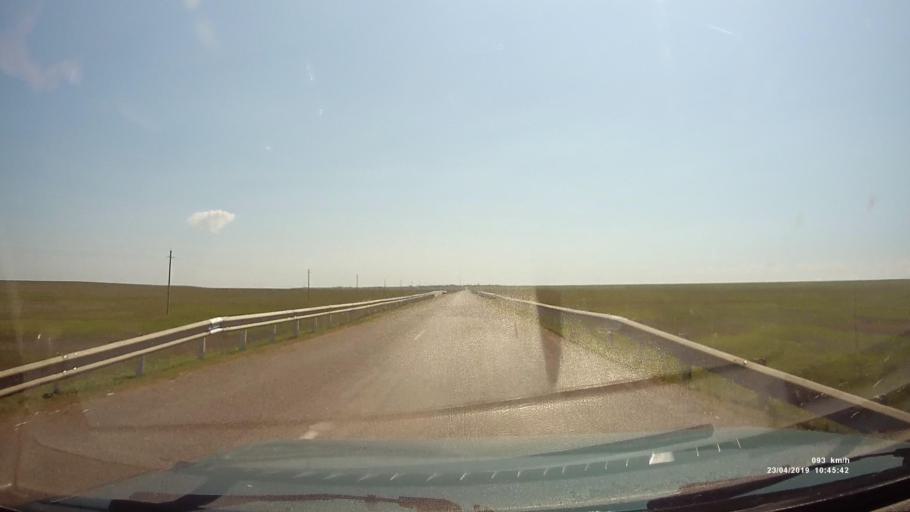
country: RU
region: Kalmykiya
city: Yashalta
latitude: 46.4490
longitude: 42.6792
